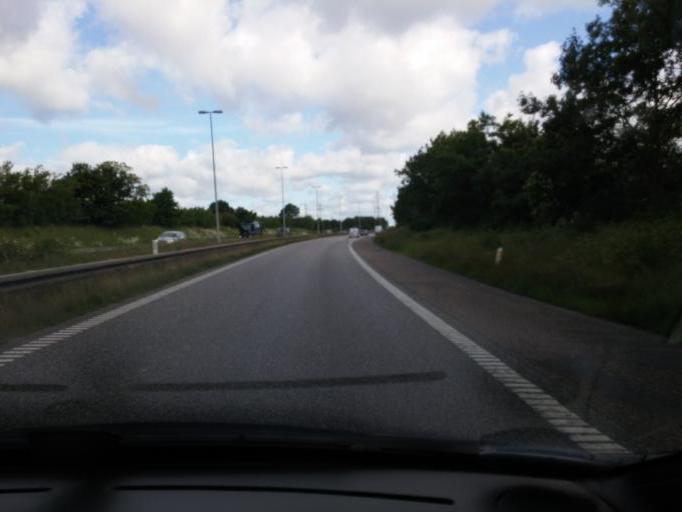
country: DK
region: Capital Region
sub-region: Brondby Kommune
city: Brondbyvester
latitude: 55.6279
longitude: 12.4324
